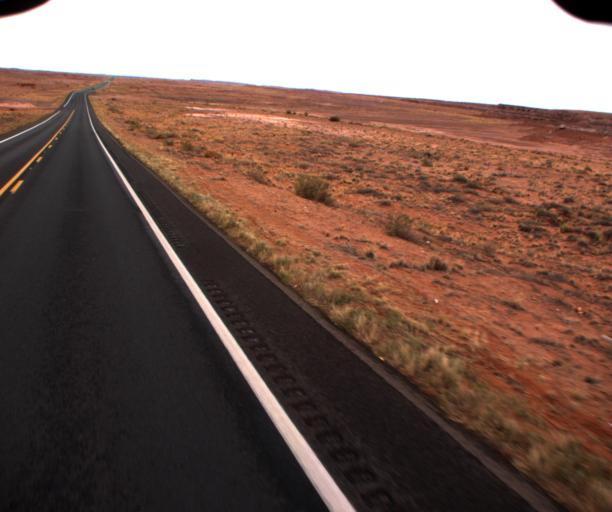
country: US
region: Arizona
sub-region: Coconino County
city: Tuba City
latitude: 36.1025
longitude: -111.2904
